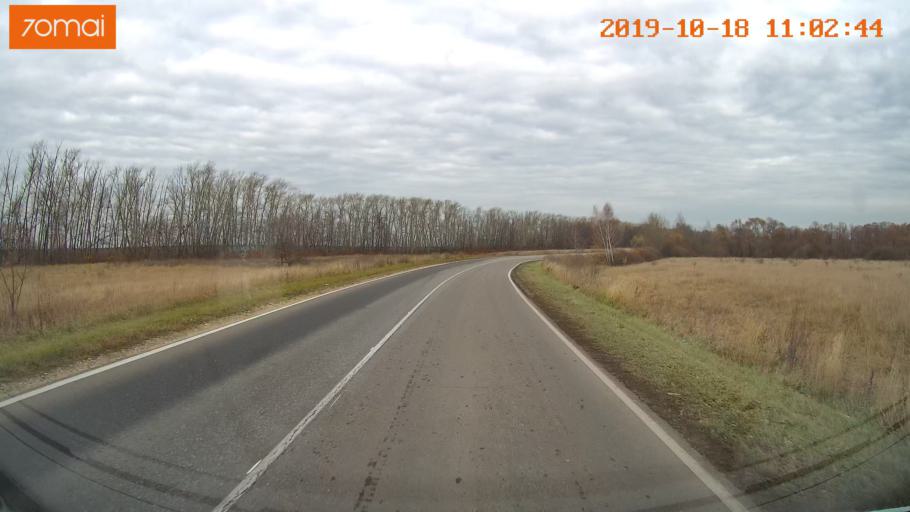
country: RU
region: Tula
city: Yepifan'
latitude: 53.8698
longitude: 38.5434
